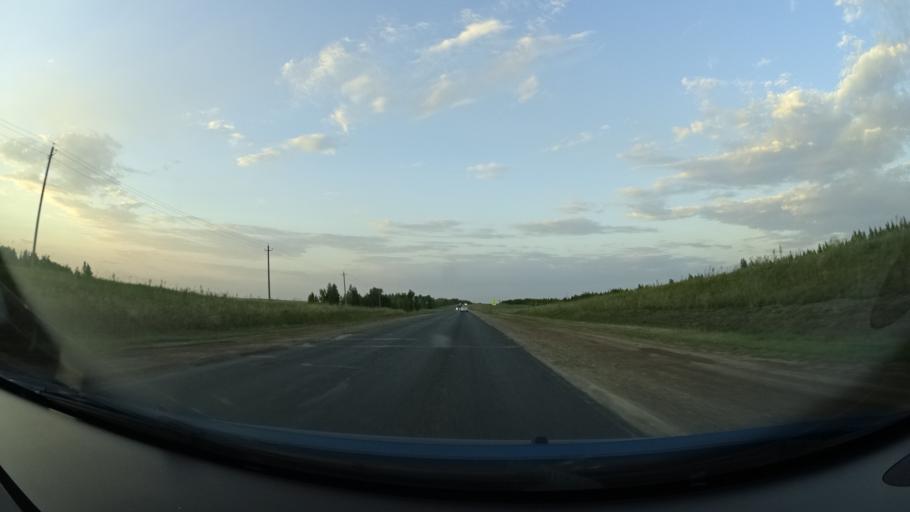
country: RU
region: Orenburg
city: Severnoye
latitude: 54.2026
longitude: 52.6921
